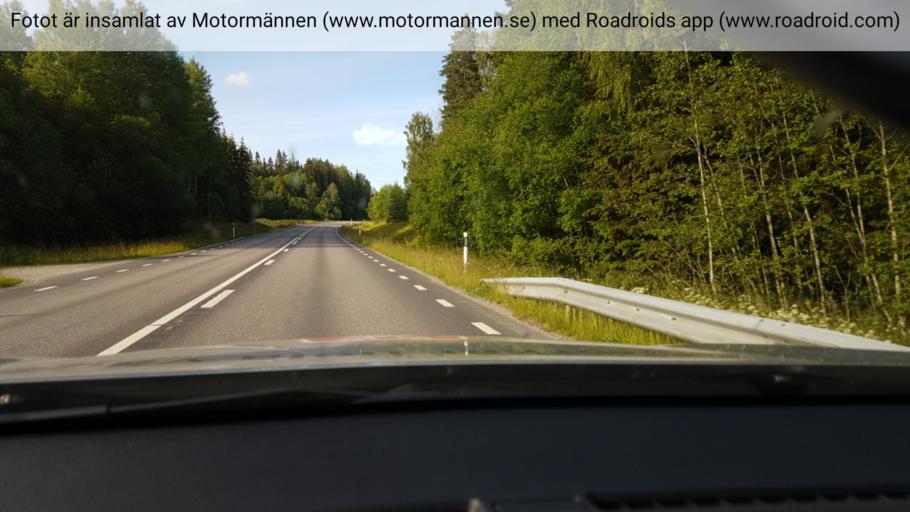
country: SE
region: Vaestra Goetaland
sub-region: Ulricehamns Kommun
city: Ulricehamn
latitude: 57.9407
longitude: 13.5101
